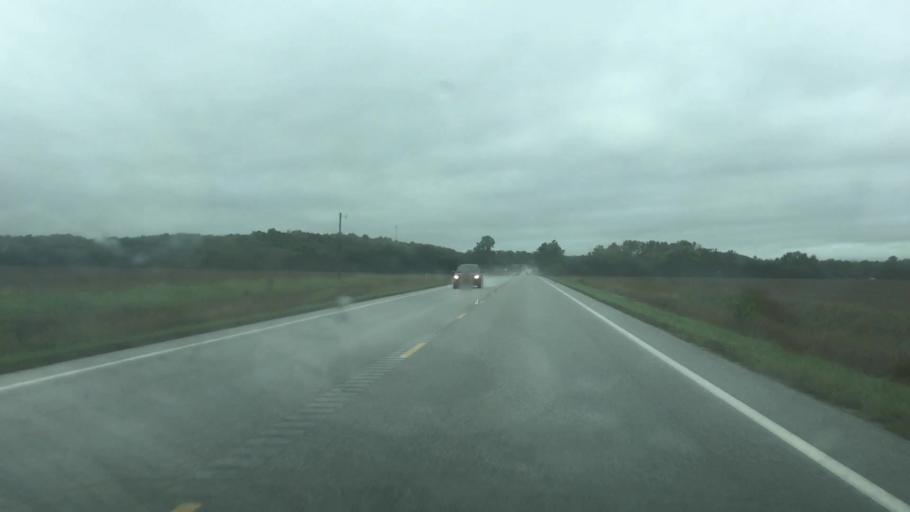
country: US
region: Kansas
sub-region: Anderson County
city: Garnett
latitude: 38.3752
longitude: -95.1146
